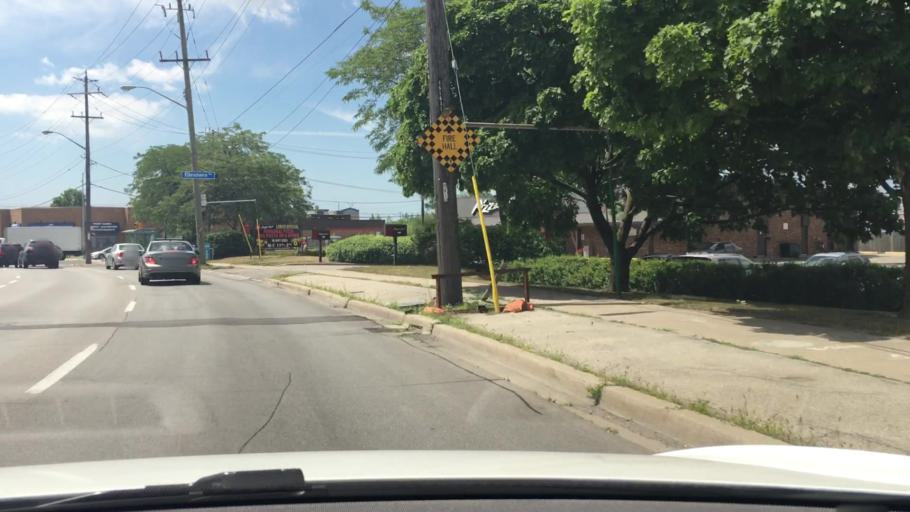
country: CA
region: Ontario
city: Scarborough
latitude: 43.7643
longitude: -79.2916
